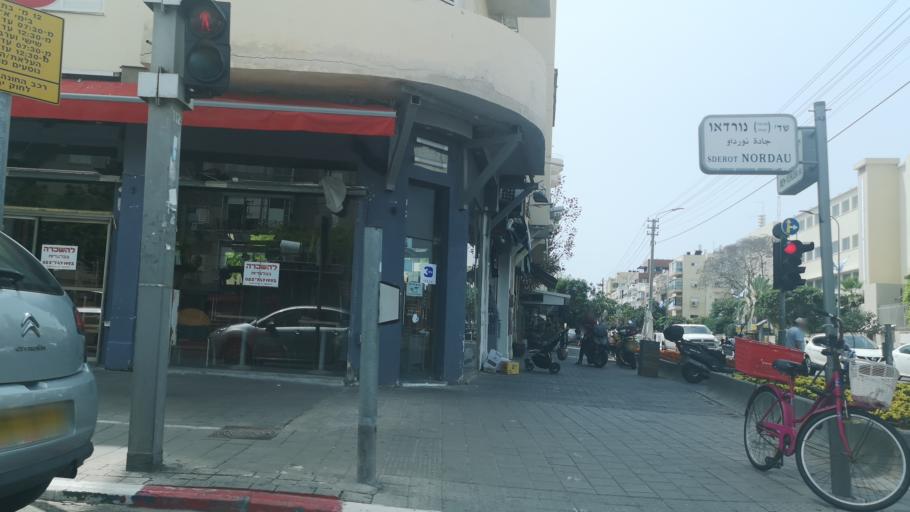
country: IL
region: Tel Aviv
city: Tel Aviv
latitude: 32.0925
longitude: 34.7747
